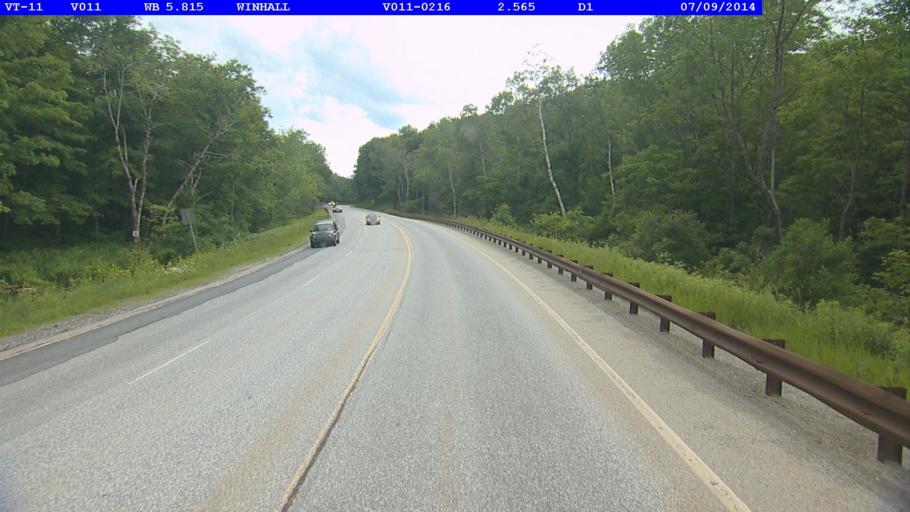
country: US
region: Vermont
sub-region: Bennington County
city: Manchester Center
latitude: 43.2067
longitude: -72.9715
